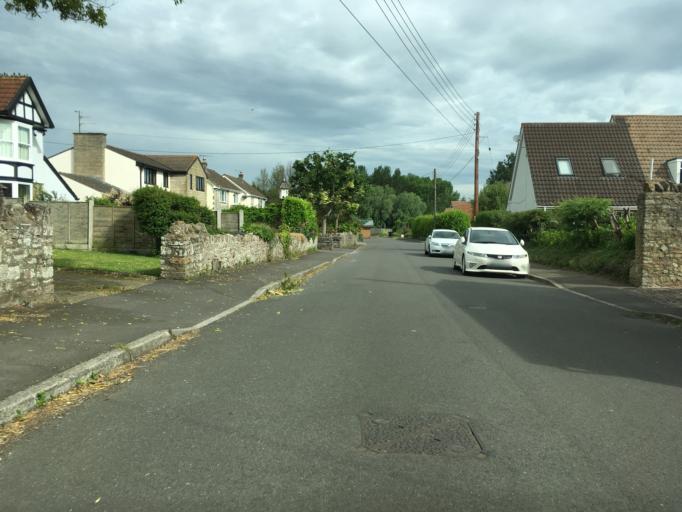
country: GB
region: England
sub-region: North Somerset
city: Easton-in-Gordano
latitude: 51.4752
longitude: -2.7245
